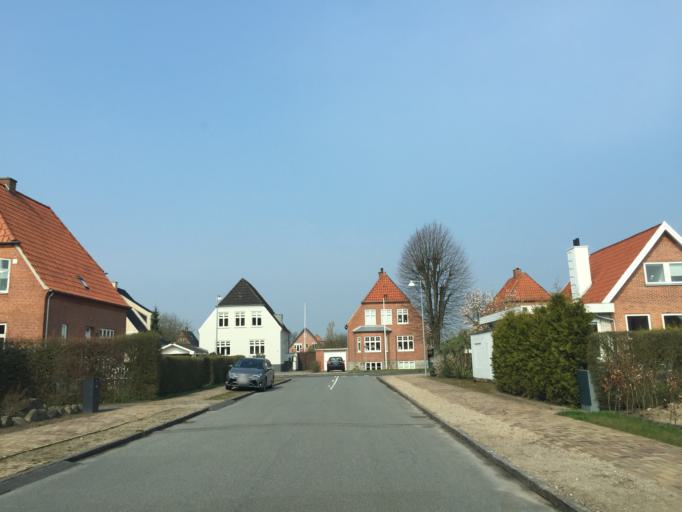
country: DK
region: South Denmark
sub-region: Odense Kommune
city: Odense
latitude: 55.4176
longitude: 10.3980
